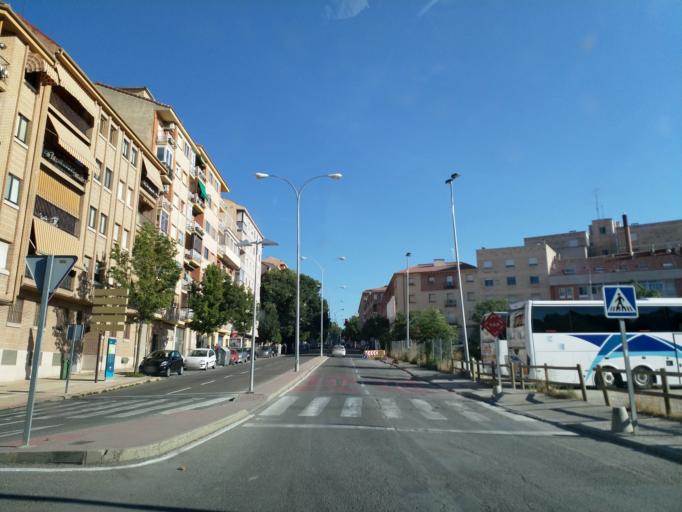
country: ES
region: Castille and Leon
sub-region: Provincia de Segovia
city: Segovia
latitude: 40.9470
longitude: -4.1240
